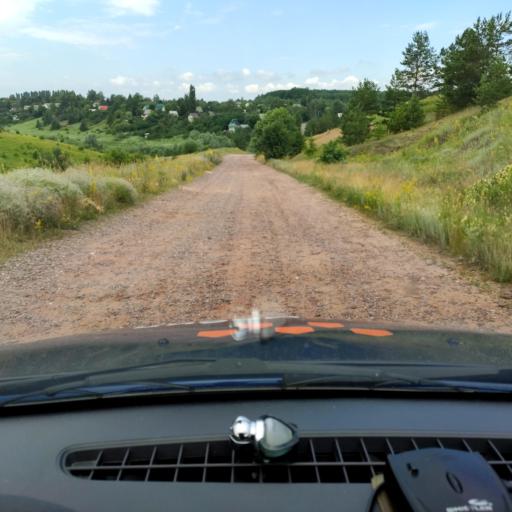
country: RU
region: Voronezj
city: Ramon'
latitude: 52.0739
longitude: 39.3210
